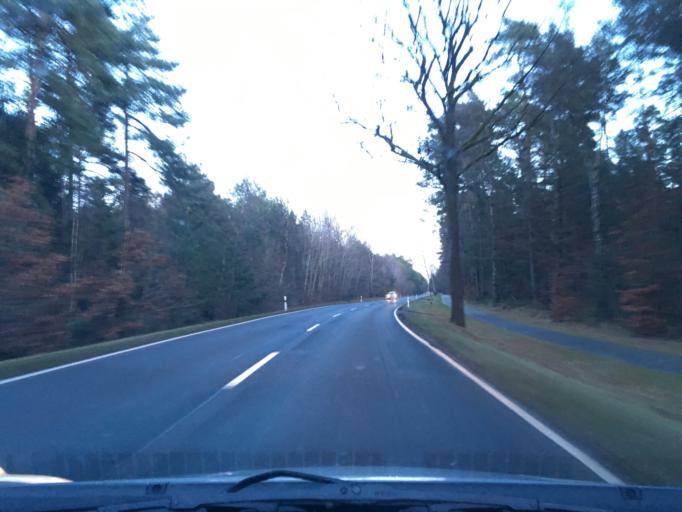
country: DE
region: Lower Saxony
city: Kusten
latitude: 52.9814
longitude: 11.0291
